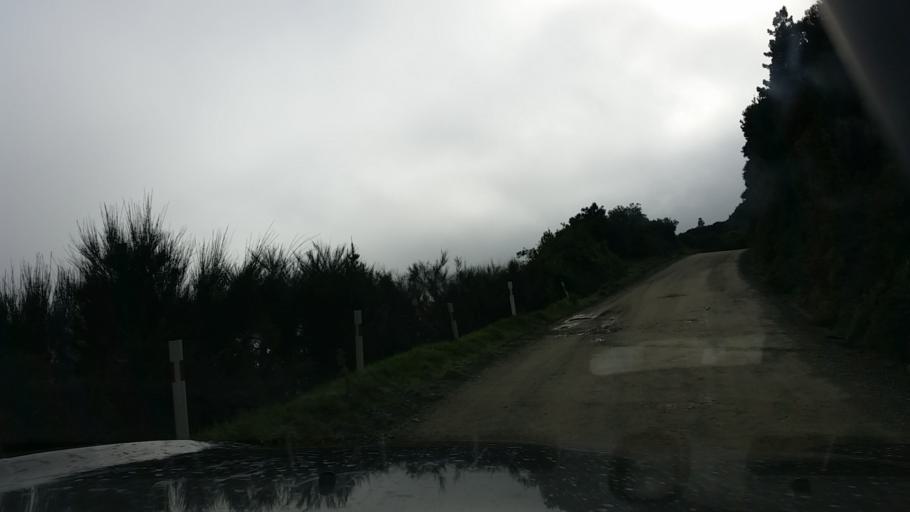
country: NZ
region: Marlborough
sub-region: Marlborough District
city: Picton
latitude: -41.1732
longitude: 174.0405
